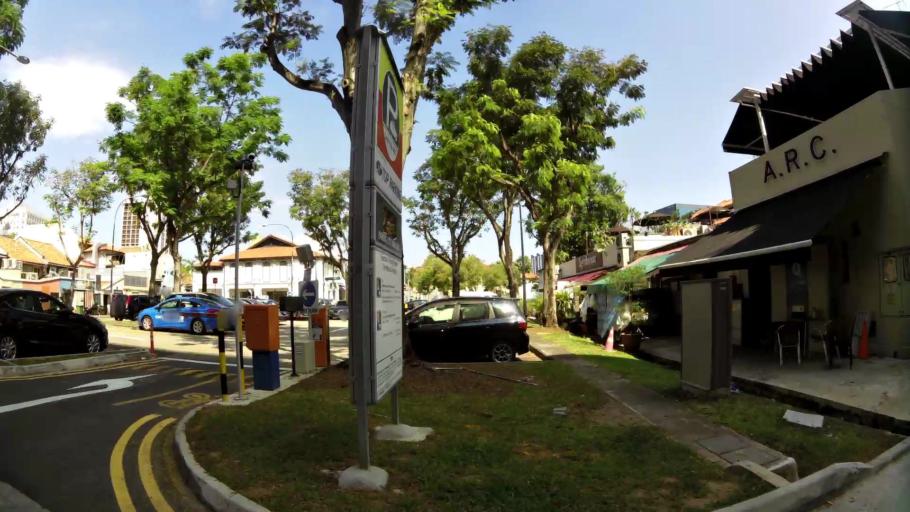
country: SG
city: Singapore
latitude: 1.3013
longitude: 103.8606
